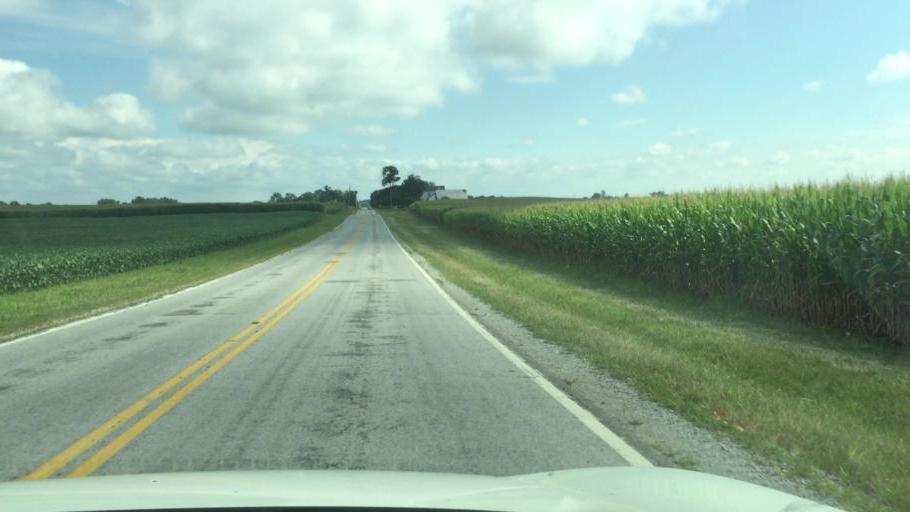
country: US
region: Ohio
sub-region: Clark County
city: Northridge
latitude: 39.9646
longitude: -83.6791
